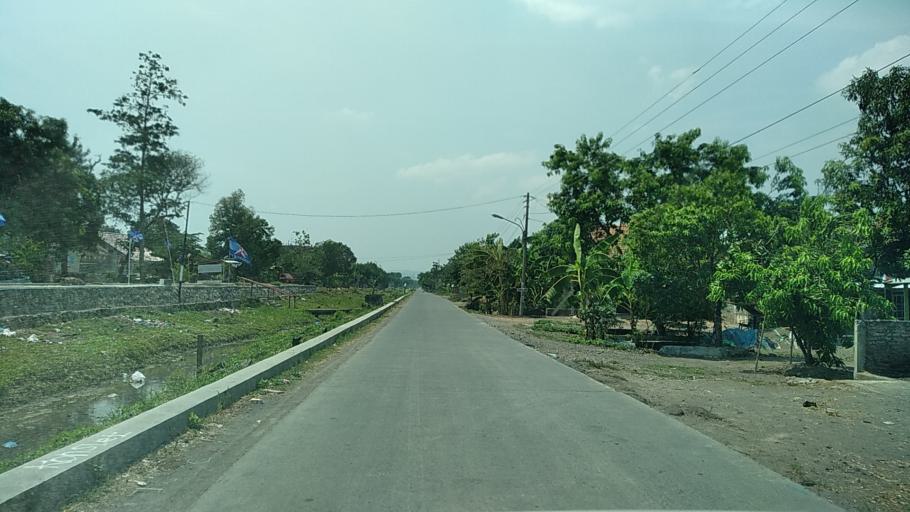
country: ID
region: Central Java
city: Mranggen
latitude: -7.0273
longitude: 110.4801
